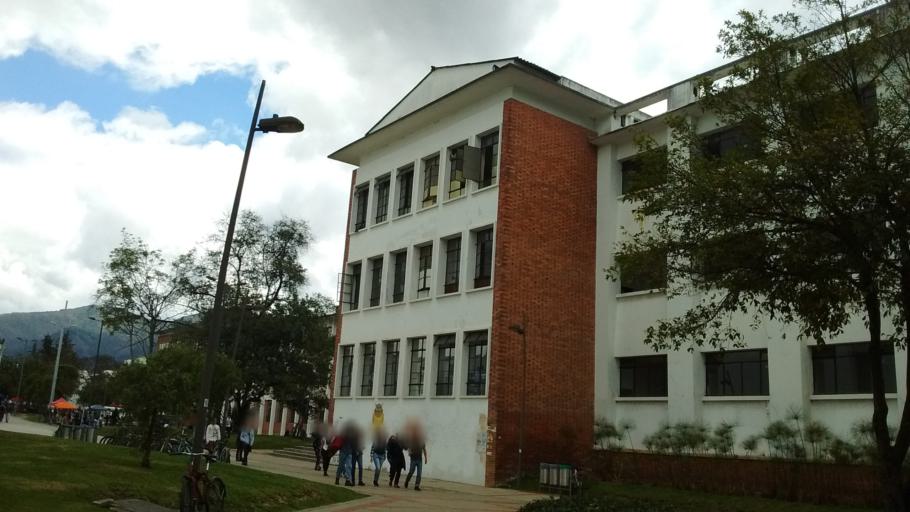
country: CO
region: Bogota D.C.
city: Bogota
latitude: 4.6376
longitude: -74.0849
